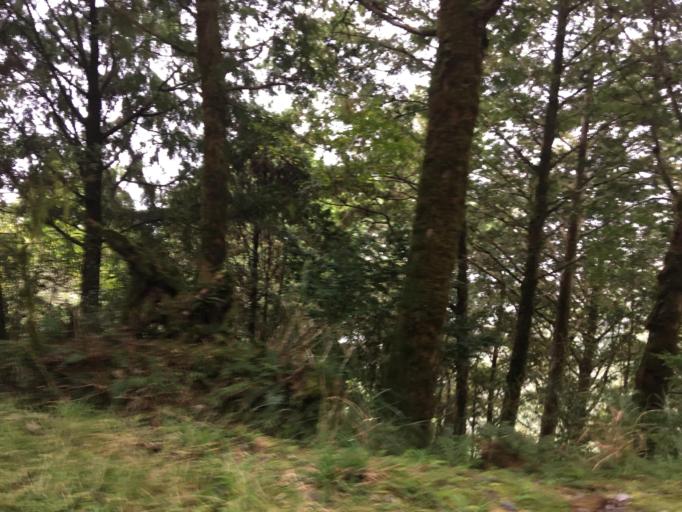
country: TW
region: Taiwan
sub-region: Yilan
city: Yilan
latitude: 24.4856
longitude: 121.5342
